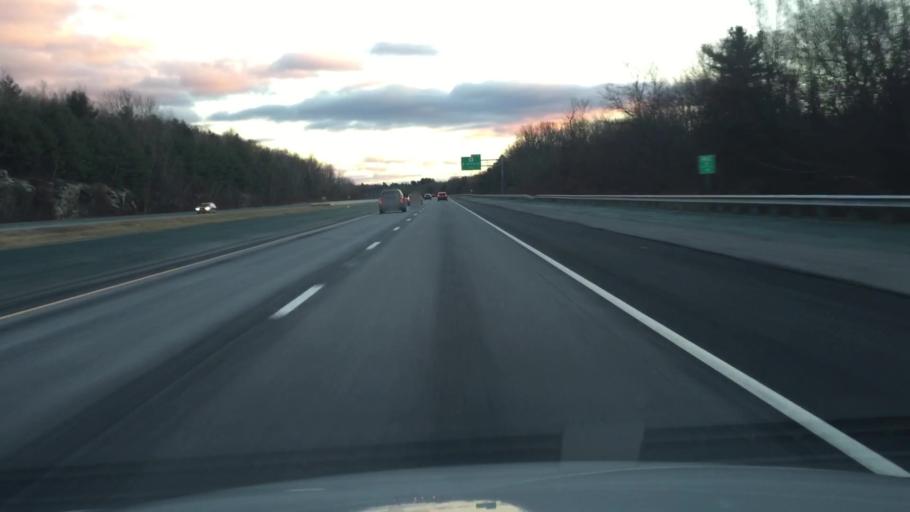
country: US
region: Massachusetts
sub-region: Worcester County
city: West Boylston
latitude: 42.3547
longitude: -71.8120
